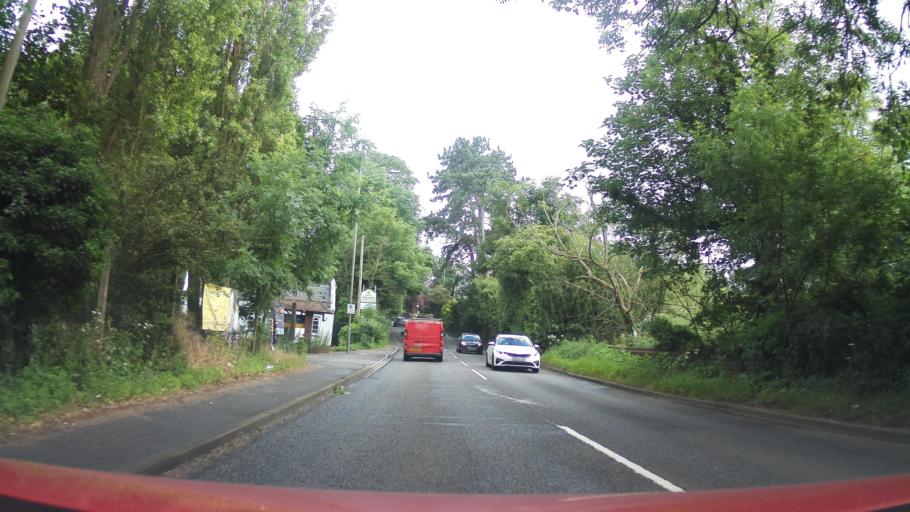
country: GB
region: England
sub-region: Dudley
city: Kingswinford
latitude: 52.5128
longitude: -2.1733
